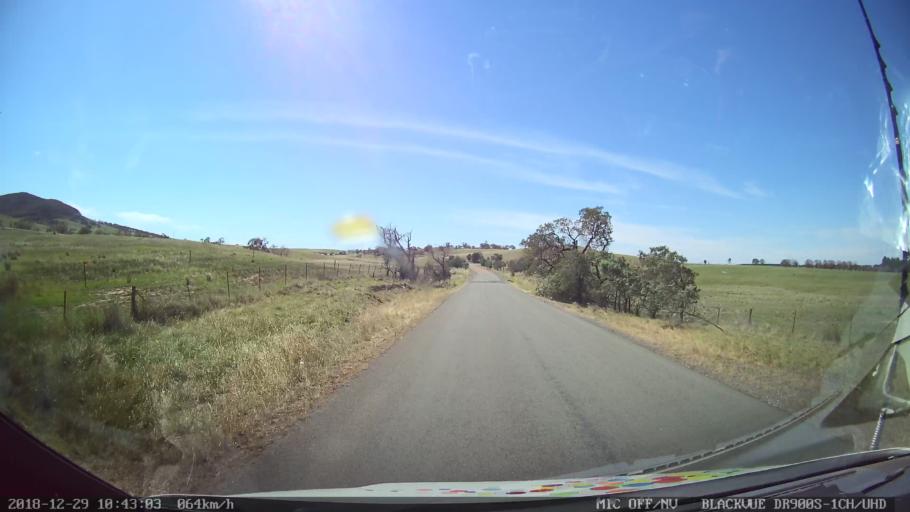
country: AU
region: New South Wales
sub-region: Palerang
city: Bungendore
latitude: -35.0380
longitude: 149.5355
